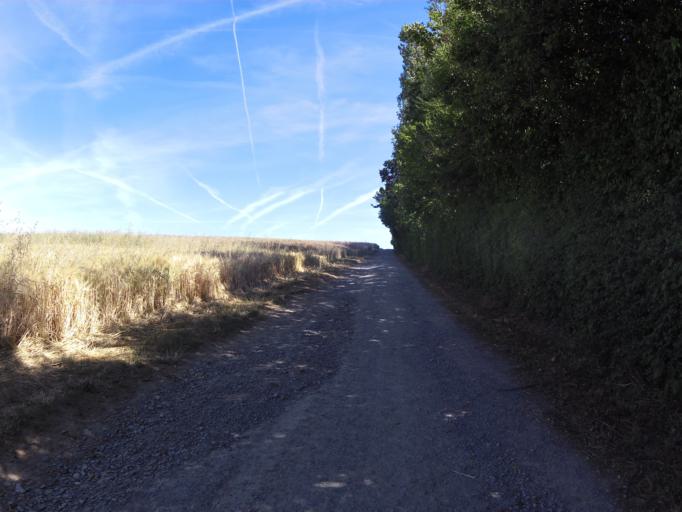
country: DE
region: Bavaria
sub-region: Regierungsbezirk Unterfranken
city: Hettstadt
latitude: 49.8079
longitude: 9.8328
